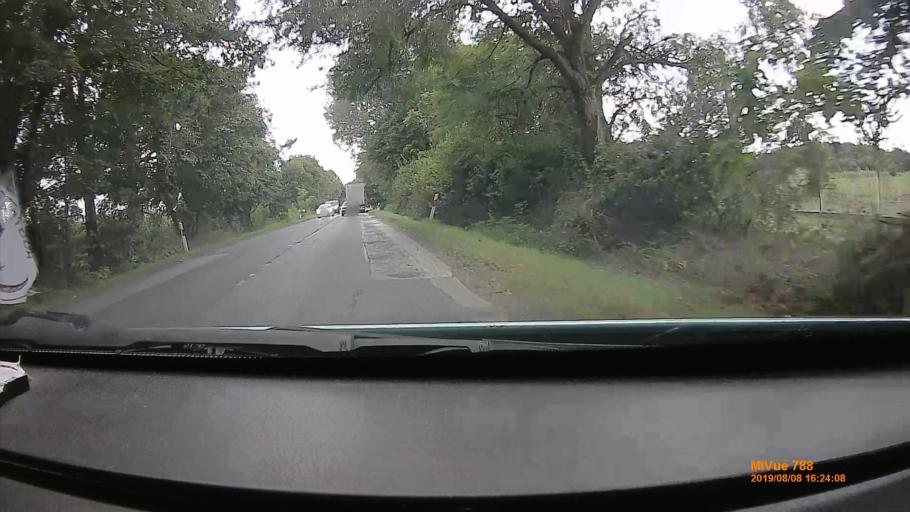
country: HU
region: Szabolcs-Szatmar-Bereg
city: Hodasz
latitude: 47.9690
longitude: 22.2309
